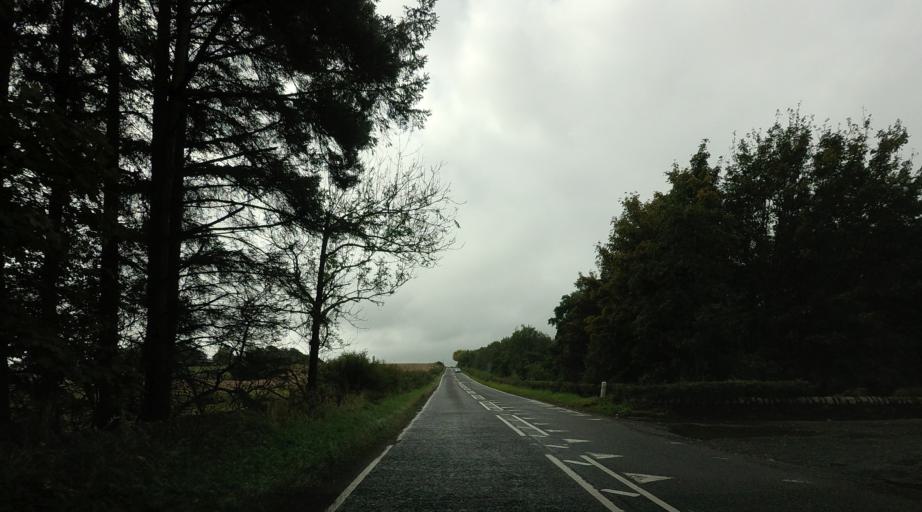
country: GB
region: Scotland
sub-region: Fife
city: Balmullo
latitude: 56.3900
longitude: -2.9081
